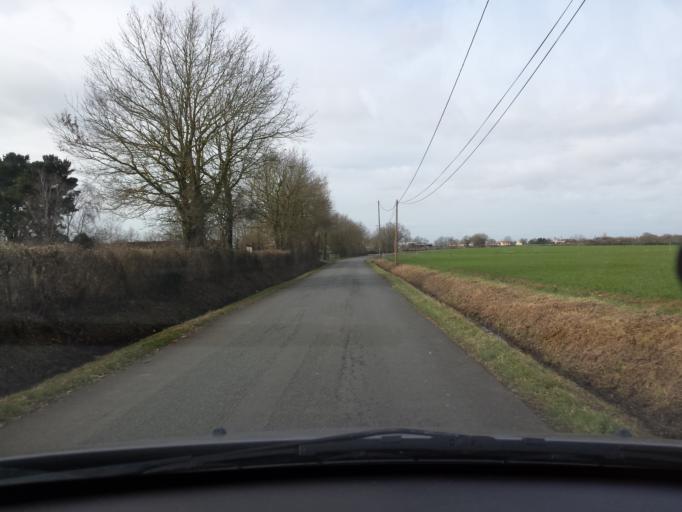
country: FR
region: Pays de la Loire
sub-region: Departement de la Vendee
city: Les Essarts
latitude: 46.7573
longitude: -1.2560
